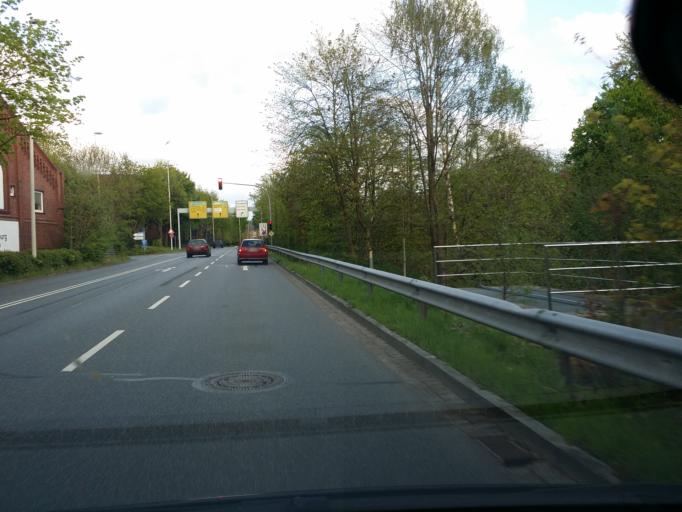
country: DE
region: Schleswig-Holstein
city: Rendsburg
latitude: 54.3033
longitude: 9.6629
